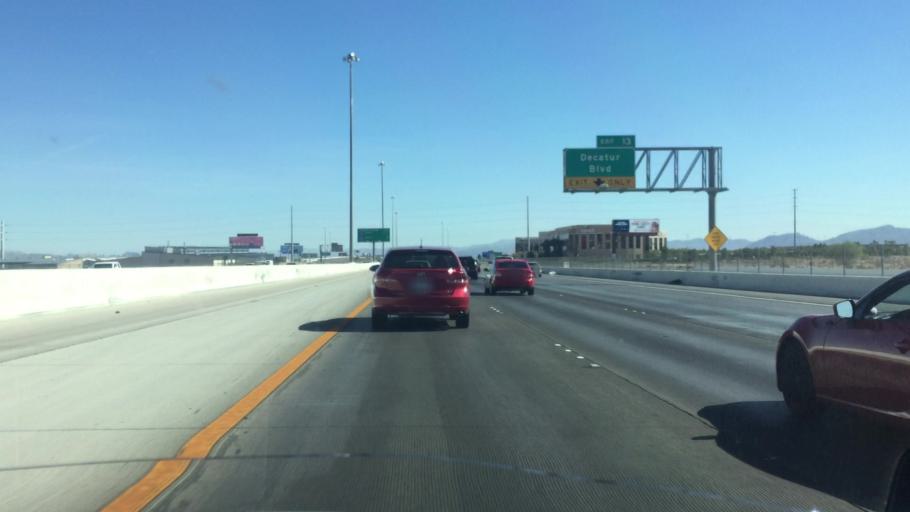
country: US
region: Nevada
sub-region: Clark County
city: Enterprise
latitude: 36.0672
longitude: -115.2185
